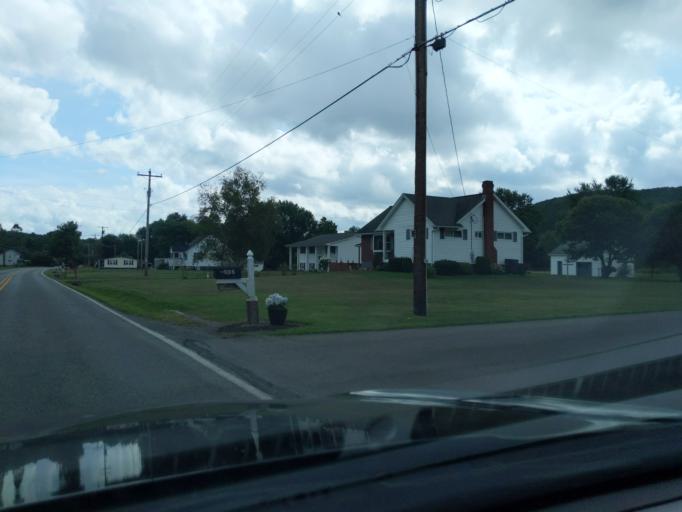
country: US
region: Pennsylvania
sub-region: Blair County
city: Duncansville
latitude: 40.3880
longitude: -78.4672
